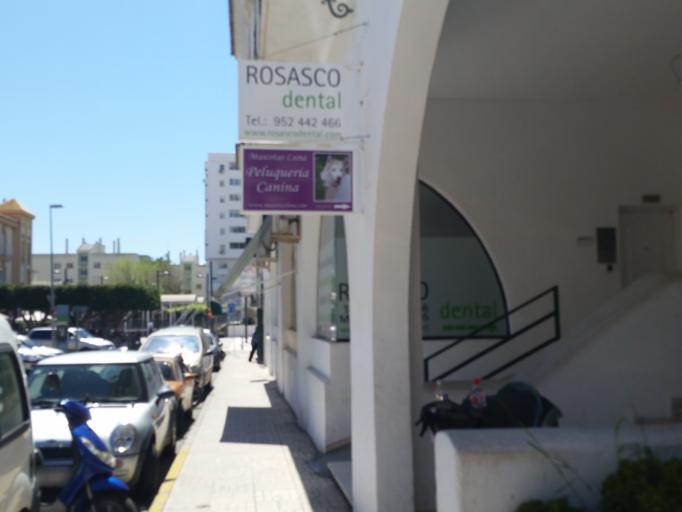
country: ES
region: Andalusia
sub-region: Provincia de Malaga
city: Benalmadena
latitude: 36.5999
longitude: -4.5366
